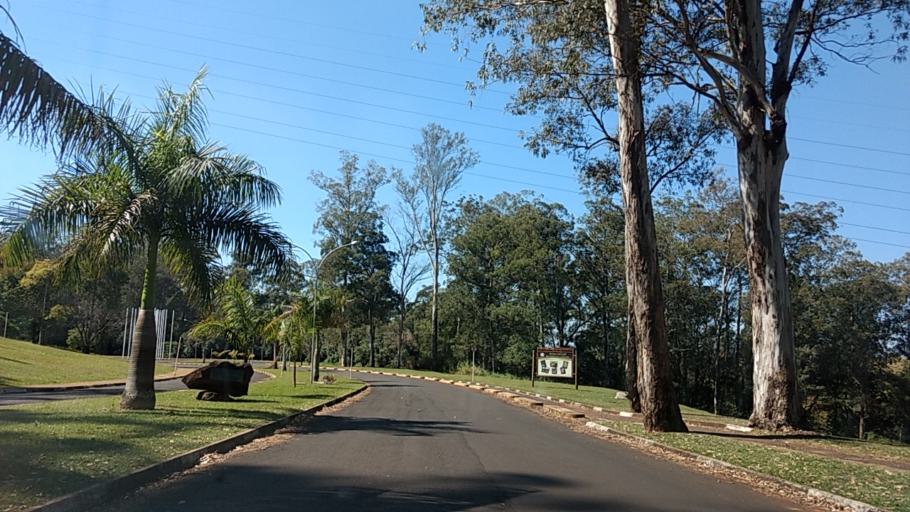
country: BR
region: Sao Paulo
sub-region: Botucatu
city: Botucatu
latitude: -22.8575
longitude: -48.4333
